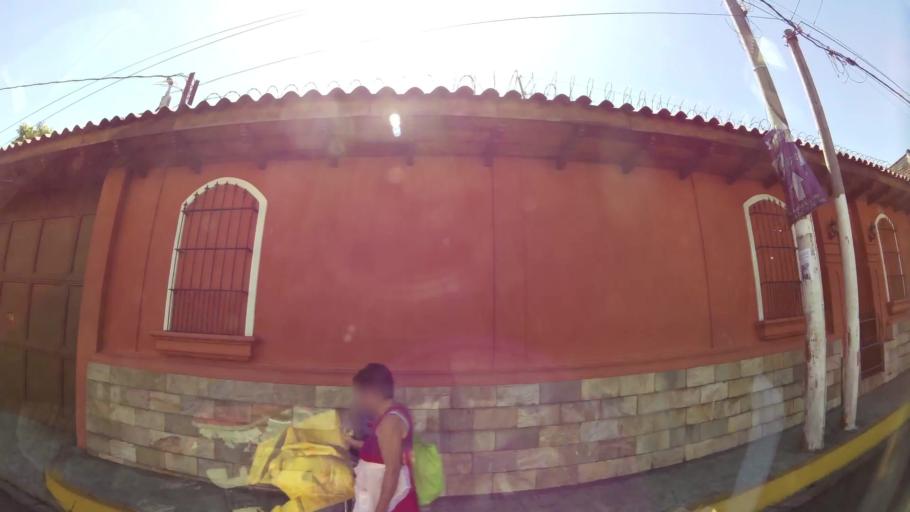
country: SV
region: San Miguel
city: San Miguel
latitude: 13.4853
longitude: -88.1729
